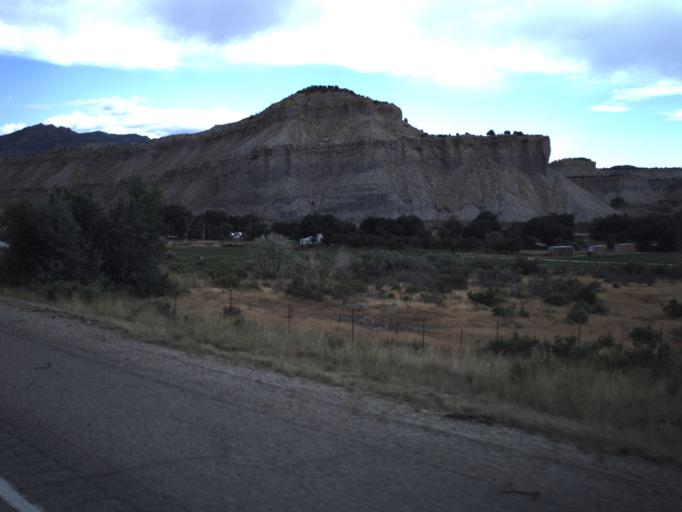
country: US
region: Utah
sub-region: Carbon County
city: Spring Glen
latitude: 39.6341
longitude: -110.8617
